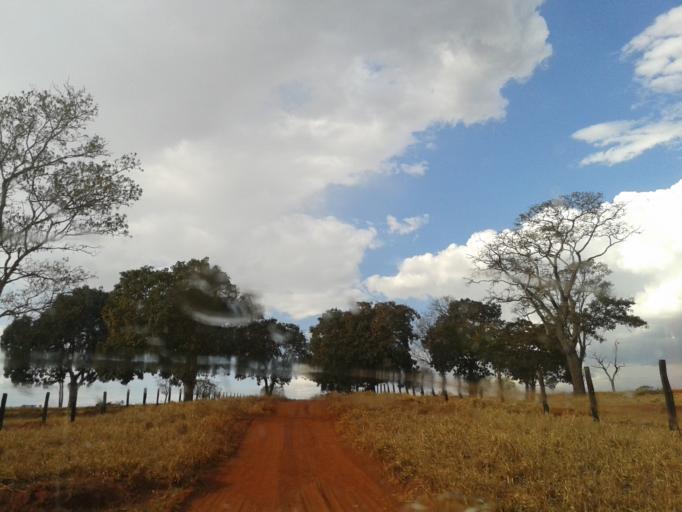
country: BR
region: Minas Gerais
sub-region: Santa Vitoria
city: Santa Vitoria
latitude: -19.1757
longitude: -49.9777
